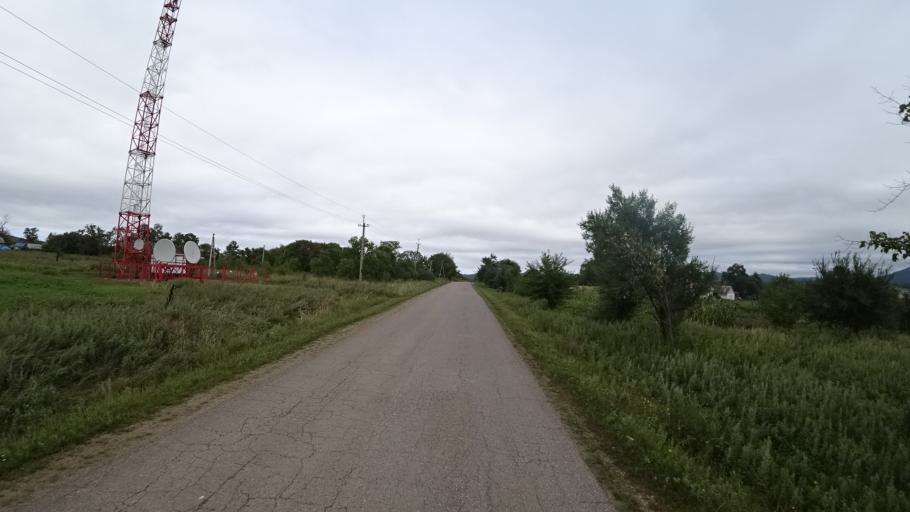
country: RU
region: Primorskiy
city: Rettikhovka
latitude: 44.1395
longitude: 132.6496
